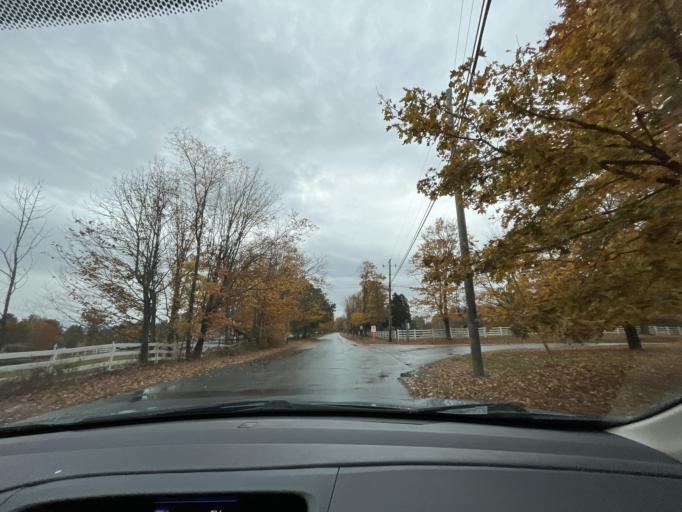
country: US
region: New Hampshire
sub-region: Merrimack County
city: New London
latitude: 43.4065
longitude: -71.9912
